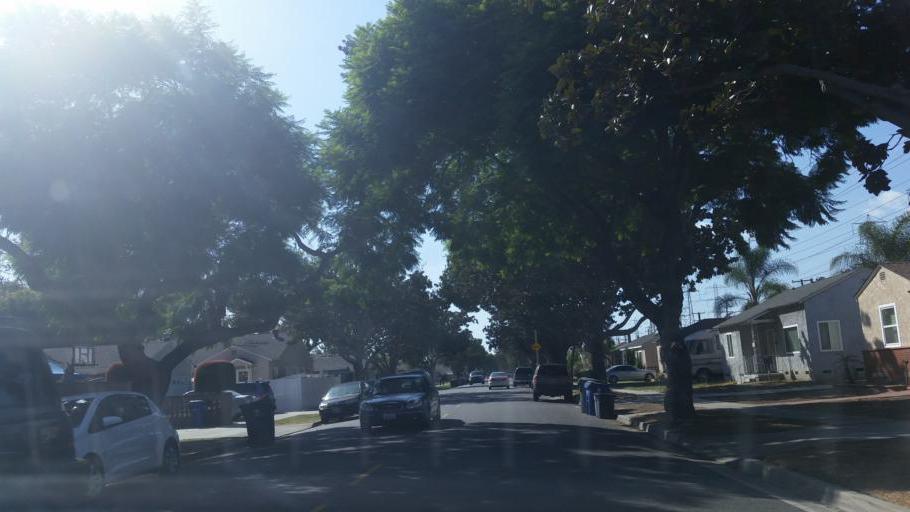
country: US
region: California
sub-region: Los Angeles County
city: Lakewood
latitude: 33.8679
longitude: -118.1264
